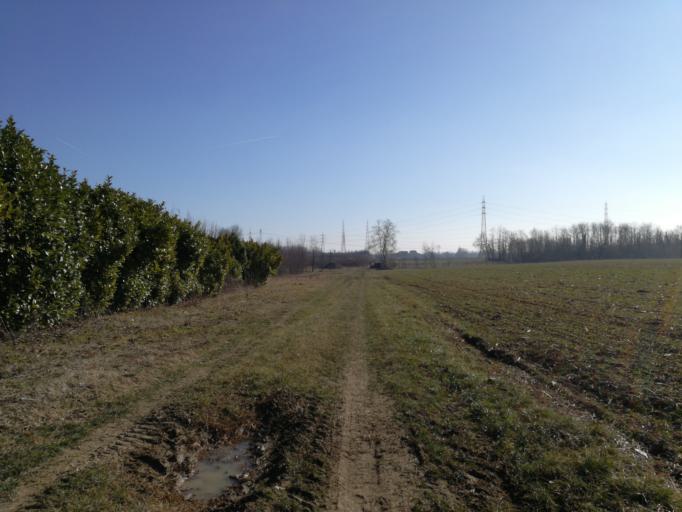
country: IT
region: Lombardy
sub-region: Provincia di Lecco
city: Verderio Inferiore
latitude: 45.6514
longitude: 9.4387
